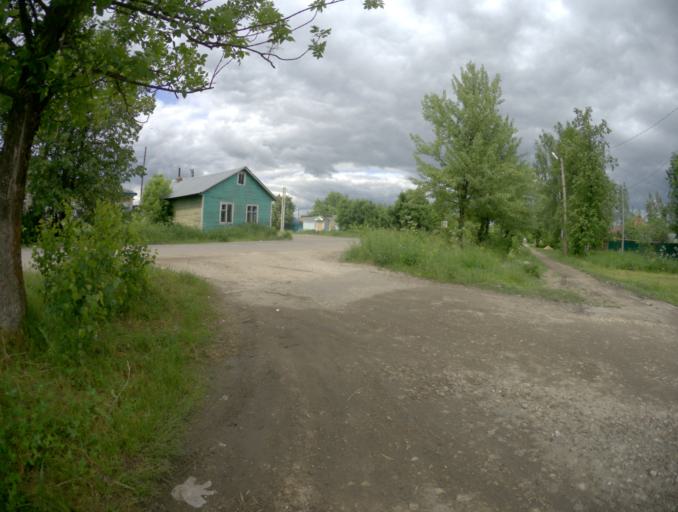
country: RU
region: Ivanovo
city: Savino
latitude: 56.5893
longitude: 41.2134
